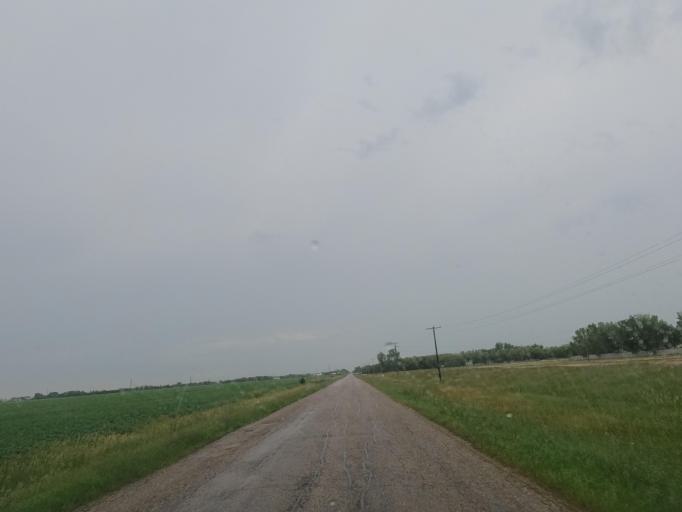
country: CA
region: Manitoba
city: Winnipeg
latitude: 49.8309
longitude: -96.9813
